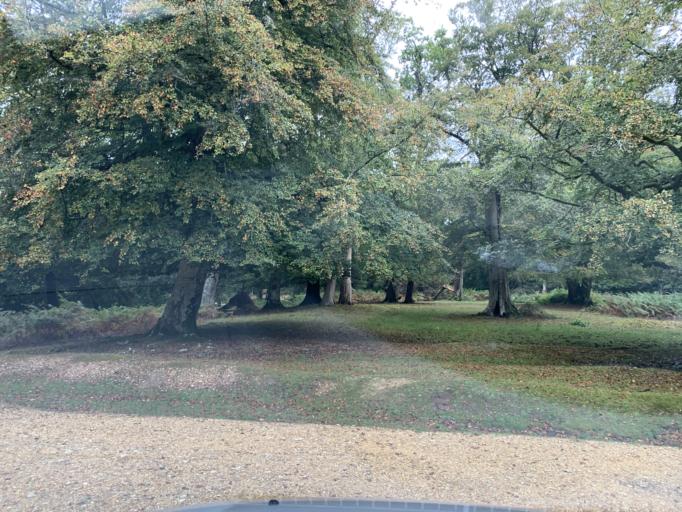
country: GB
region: England
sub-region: Hampshire
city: Lyndhurst
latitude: 50.8639
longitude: -1.6497
